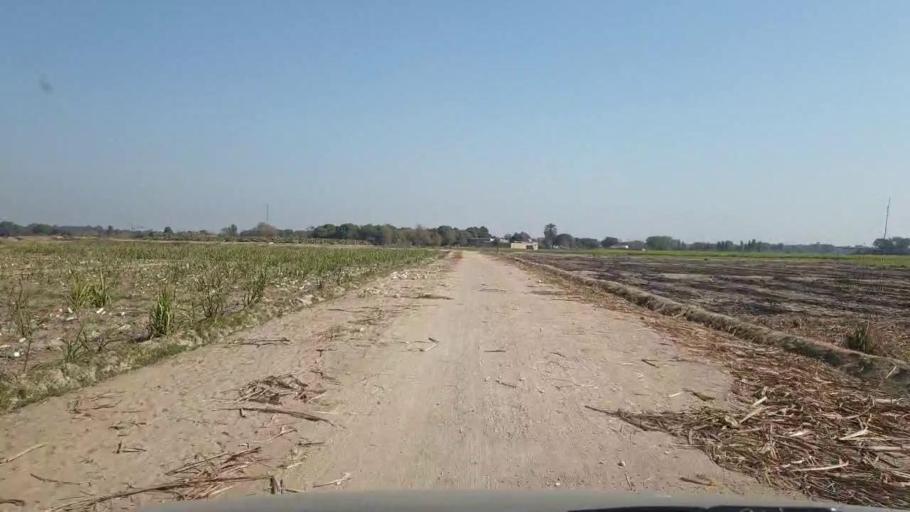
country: PK
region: Sindh
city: Tando Jam
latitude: 25.4404
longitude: 68.6185
